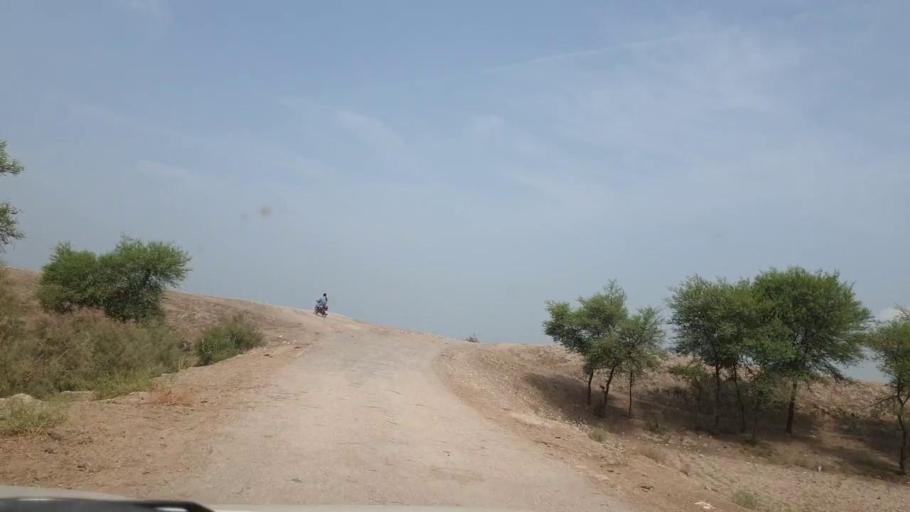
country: PK
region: Sindh
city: Dokri
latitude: 27.4058
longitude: 68.2438
